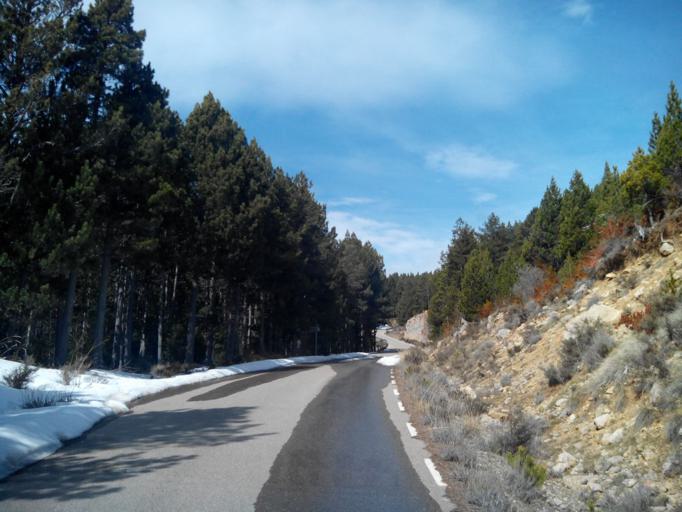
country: ES
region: Catalonia
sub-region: Provincia de Barcelona
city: Vallcebre
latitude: 42.2002
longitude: 1.7855
